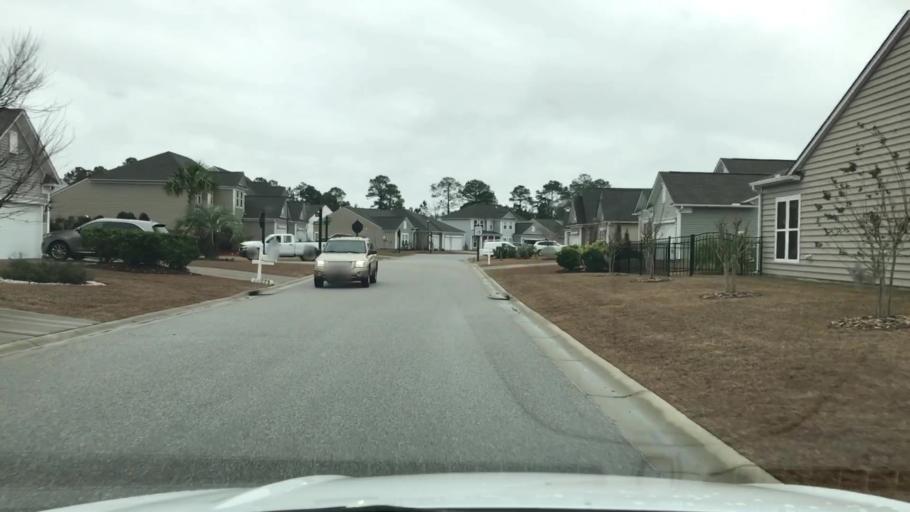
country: US
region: South Carolina
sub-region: Horry County
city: Forestbrook
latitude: 33.7462
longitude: -78.9049
